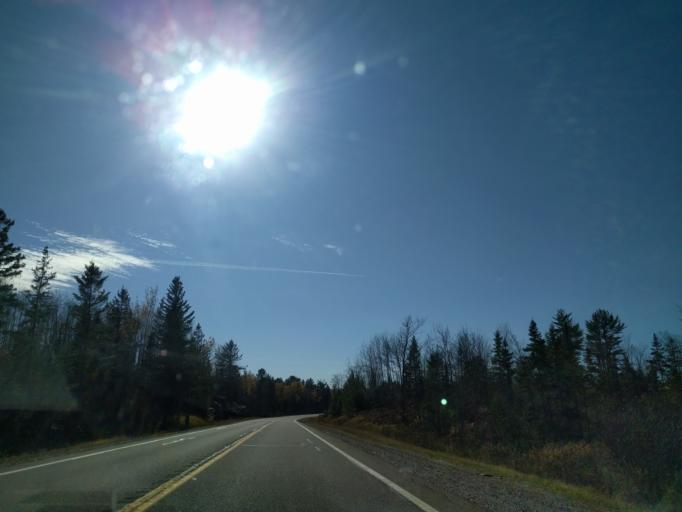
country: US
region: Michigan
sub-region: Marquette County
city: West Ishpeming
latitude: 46.4628
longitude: -87.9343
